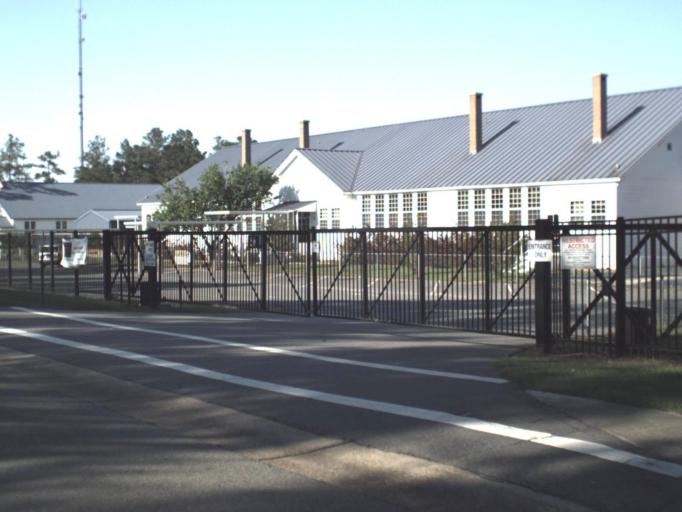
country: US
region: Florida
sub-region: Liberty County
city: Bristol
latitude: 30.3883
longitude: -84.7984
